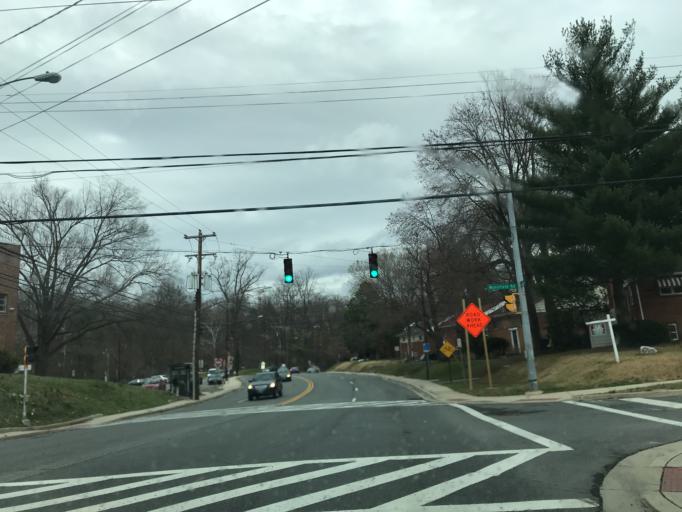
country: US
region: Maryland
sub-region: Montgomery County
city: Silver Spring
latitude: 38.9998
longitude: -77.0137
